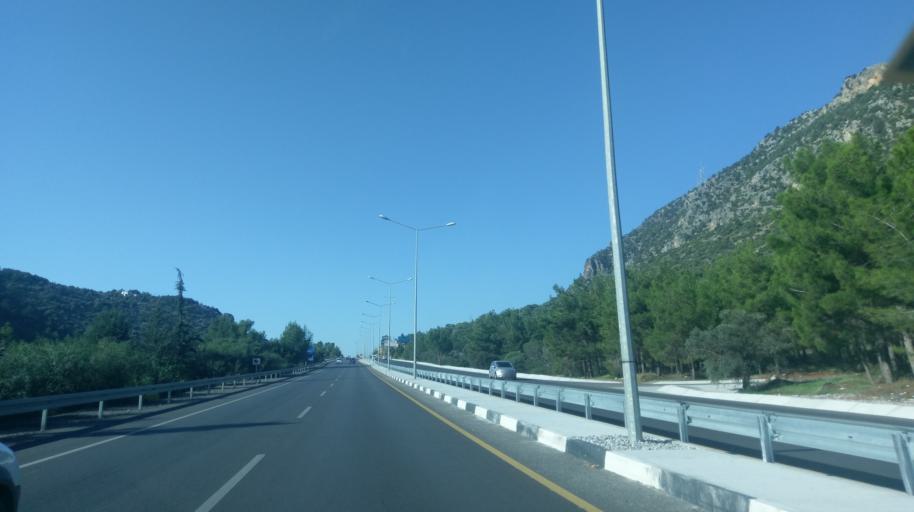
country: CY
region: Keryneia
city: Kyrenia
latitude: 35.3041
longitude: 33.2958
